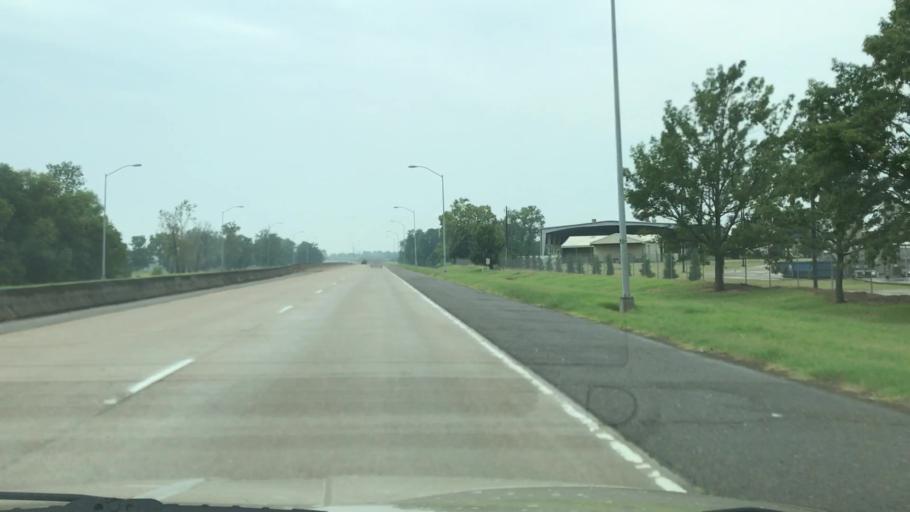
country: US
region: Louisiana
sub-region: Bossier Parish
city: Bossier City
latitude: 32.4825
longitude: -93.6842
